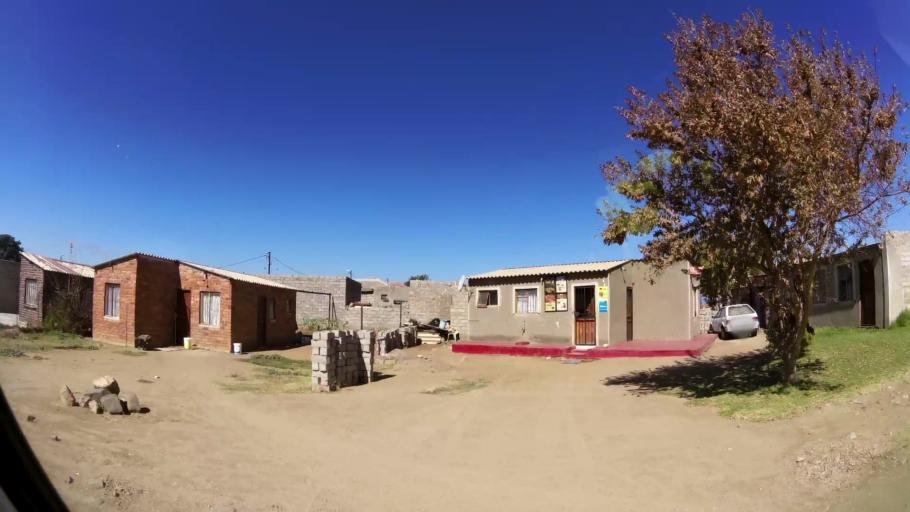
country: ZA
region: Limpopo
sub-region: Capricorn District Municipality
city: Polokwane
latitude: -23.8892
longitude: 29.4179
